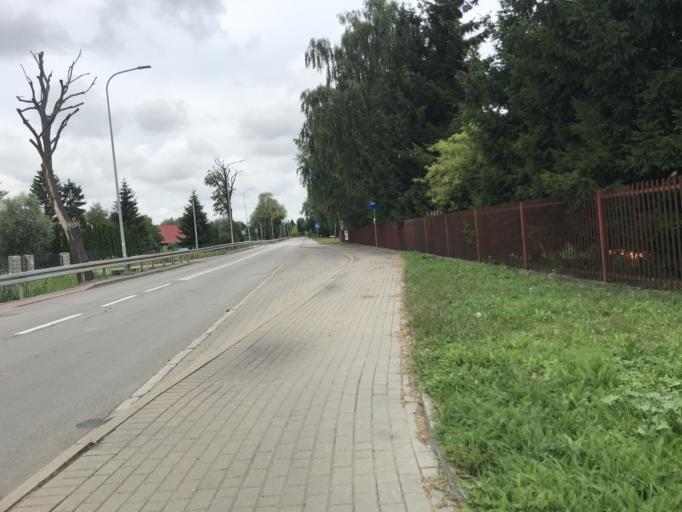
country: PL
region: Warmian-Masurian Voivodeship
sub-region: Powiat elblaski
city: Elblag
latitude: 54.1673
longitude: 19.3888
